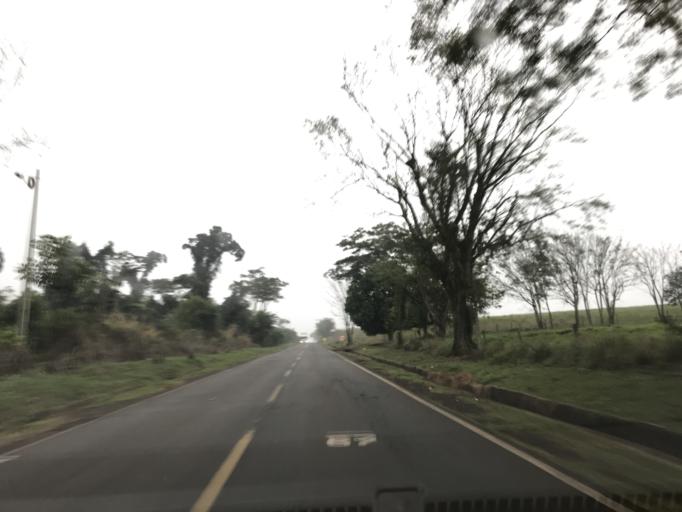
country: PY
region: Canindeyu
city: Salto del Guaira
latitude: -24.0920
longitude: -54.0951
